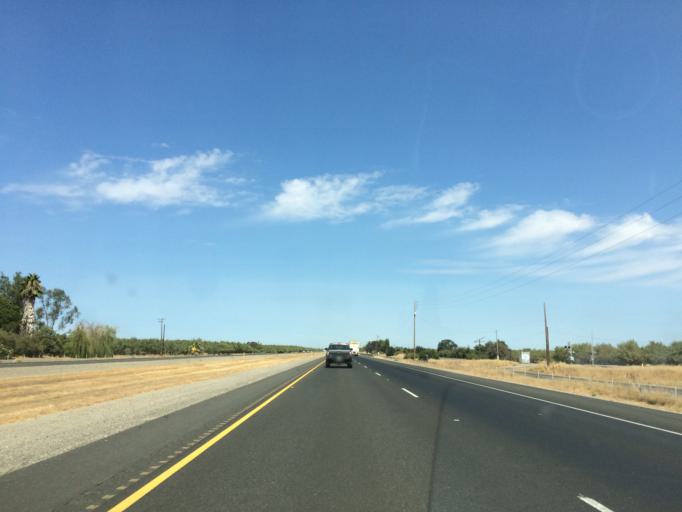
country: US
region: California
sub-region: Colusa County
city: Arbuckle
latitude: 38.9826
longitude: -122.0343
